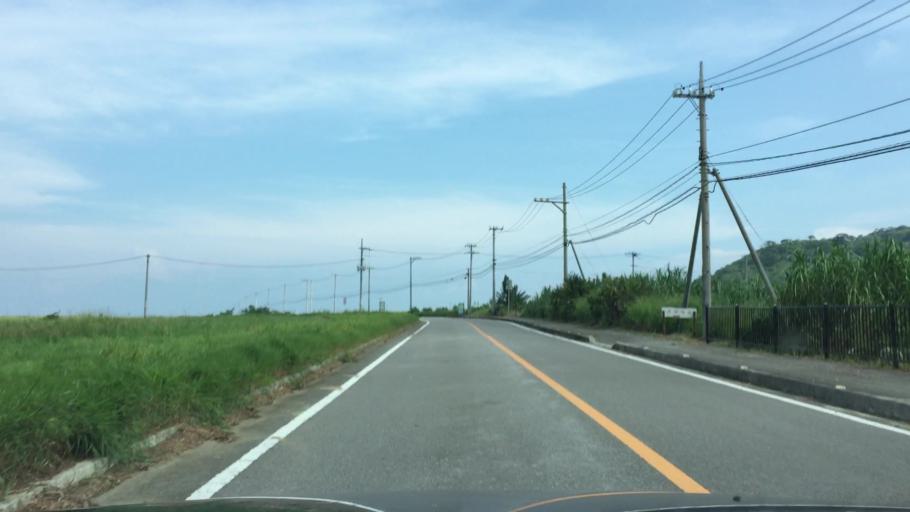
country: JP
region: Okinawa
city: Ishigaki
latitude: 24.5074
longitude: 124.2705
